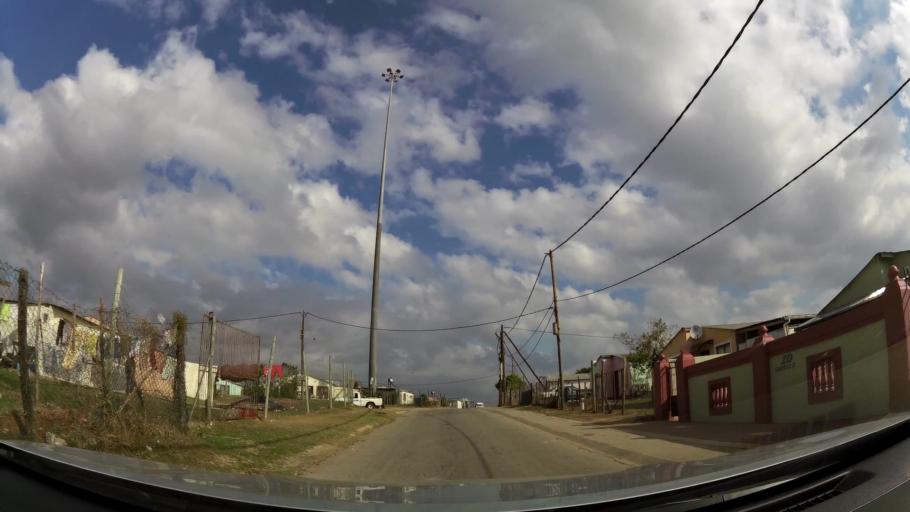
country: ZA
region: Eastern Cape
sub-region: Nelson Mandela Bay Metropolitan Municipality
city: Uitenhage
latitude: -33.7449
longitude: 25.3969
